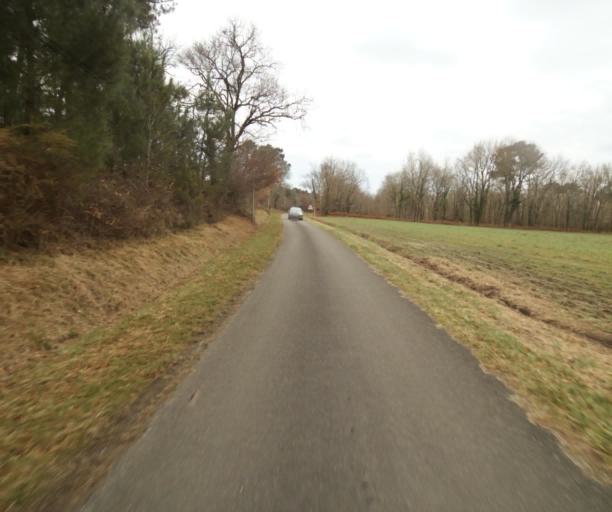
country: FR
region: Aquitaine
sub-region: Departement des Landes
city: Gabarret
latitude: 44.0171
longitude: -0.0609
